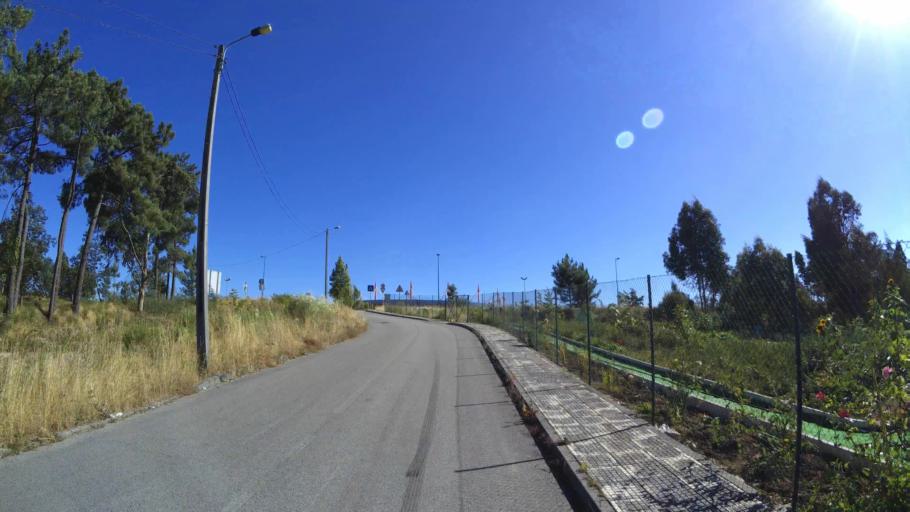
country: PT
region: Aveiro
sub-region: Aveiro
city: Eixo
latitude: 40.6518
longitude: -8.5921
